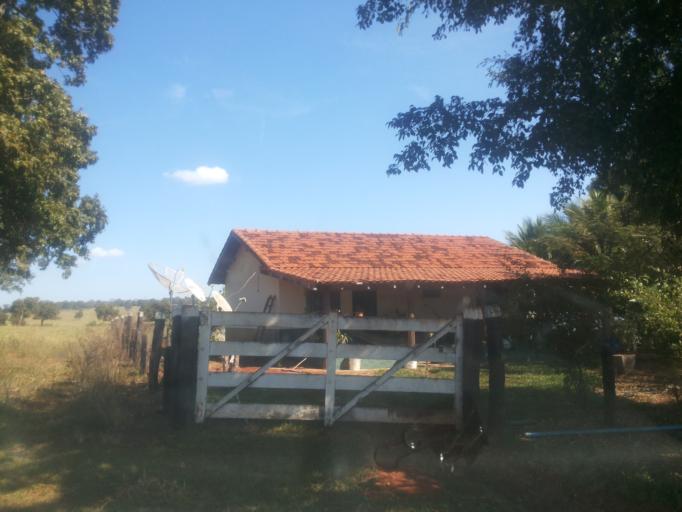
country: BR
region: Minas Gerais
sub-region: Santa Vitoria
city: Santa Vitoria
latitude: -19.0100
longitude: -50.4151
